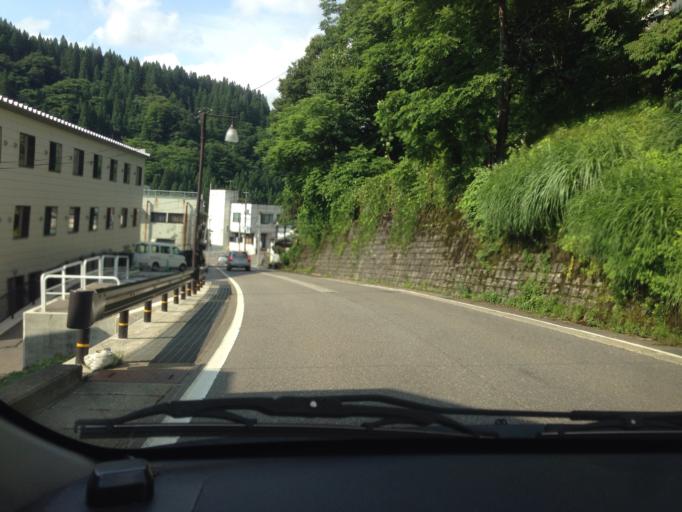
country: JP
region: Fukushima
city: Kitakata
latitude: 37.4538
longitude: 139.5237
